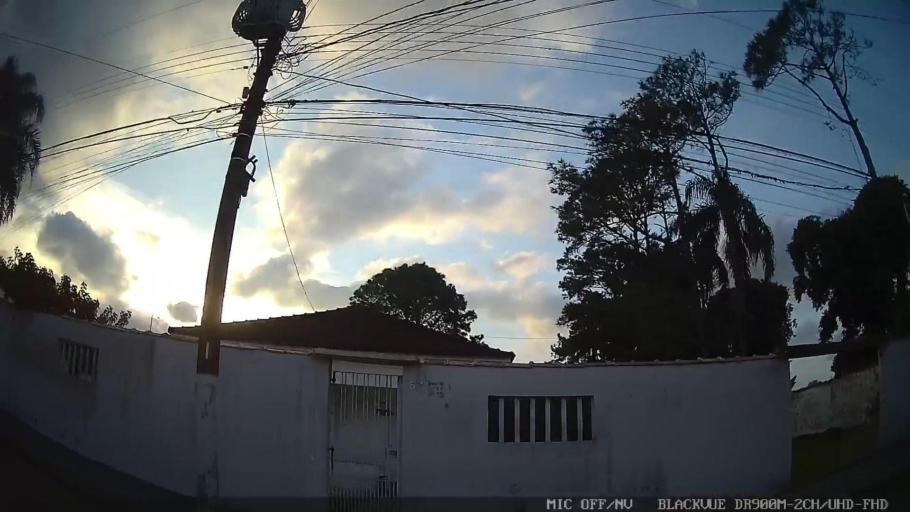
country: BR
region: Sao Paulo
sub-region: Peruibe
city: Peruibe
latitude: -24.3161
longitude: -47.0019
